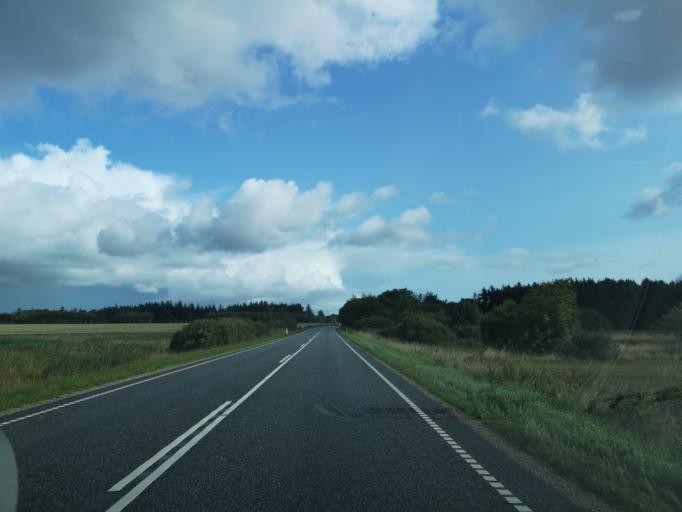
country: DK
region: Central Jutland
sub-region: Ringkobing-Skjern Kommune
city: Videbaek
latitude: 56.0359
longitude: 8.6101
